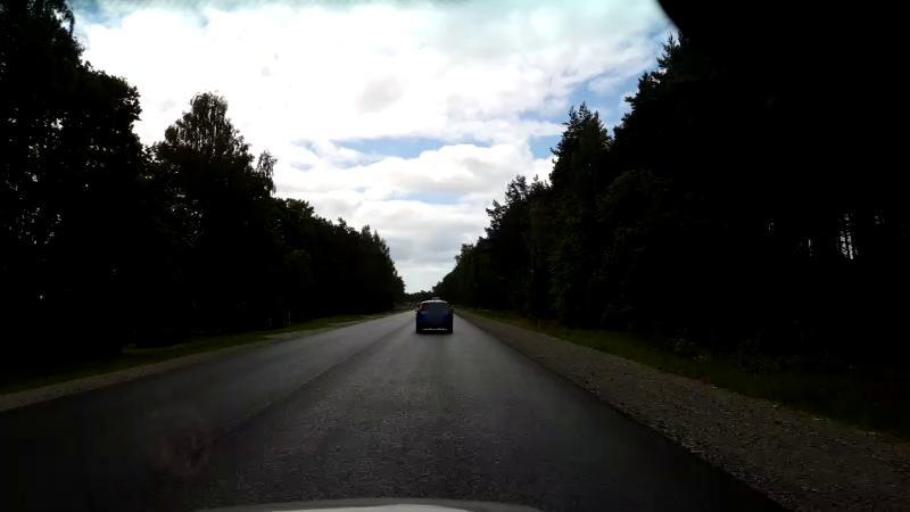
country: LV
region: Salacgrivas
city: Ainazi
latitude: 57.8384
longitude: 24.3470
